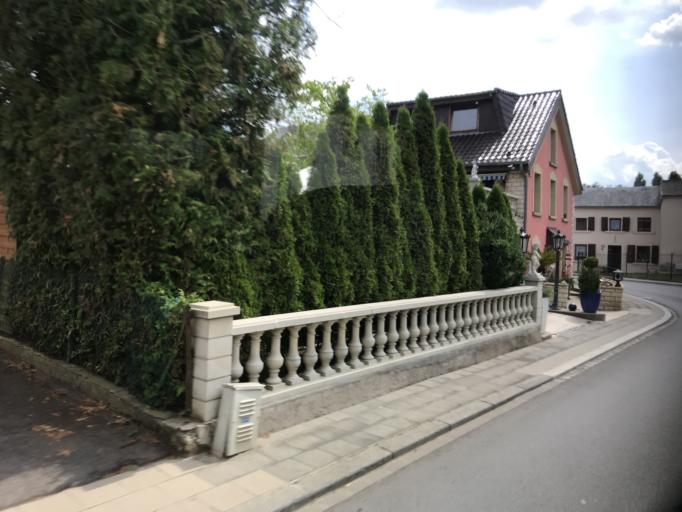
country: LU
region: Luxembourg
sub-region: Canton d'Esch-sur-Alzette
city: Bettembourg
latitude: 49.5286
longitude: 6.1198
